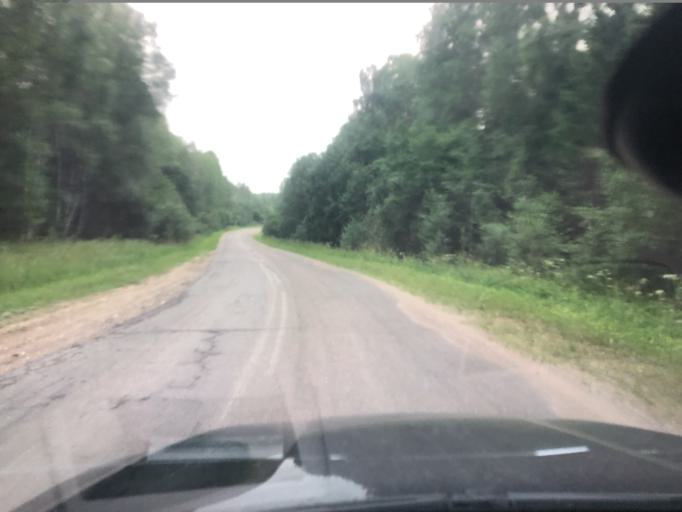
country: RU
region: Jaroslavl
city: Petrovsk
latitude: 56.9992
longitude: 39.0894
